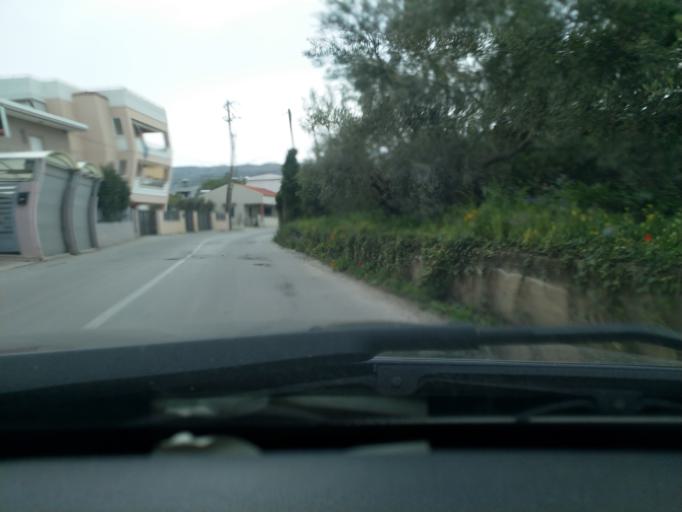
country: GR
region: Crete
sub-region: Nomos Chanias
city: Chania
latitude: 35.4985
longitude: 24.0216
